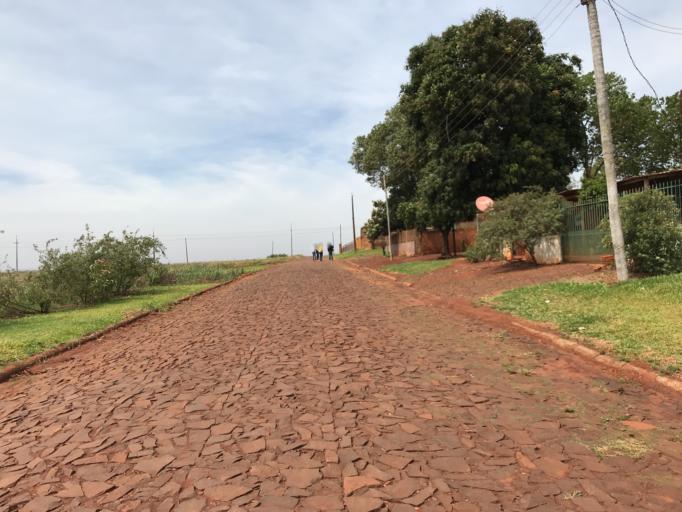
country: PY
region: Alto Parana
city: Naranjal
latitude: -25.9721
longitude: -55.2093
